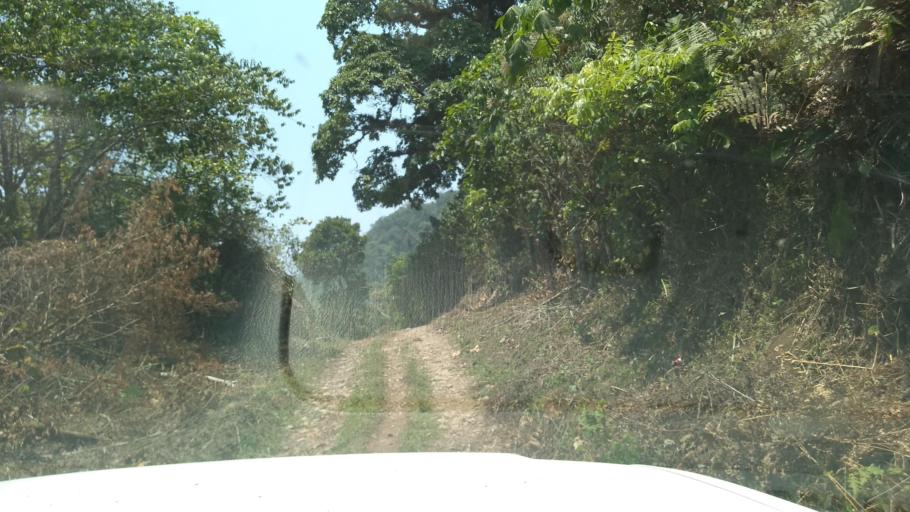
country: MX
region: Veracruz
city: Motzorongo
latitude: 18.6129
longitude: -96.7610
